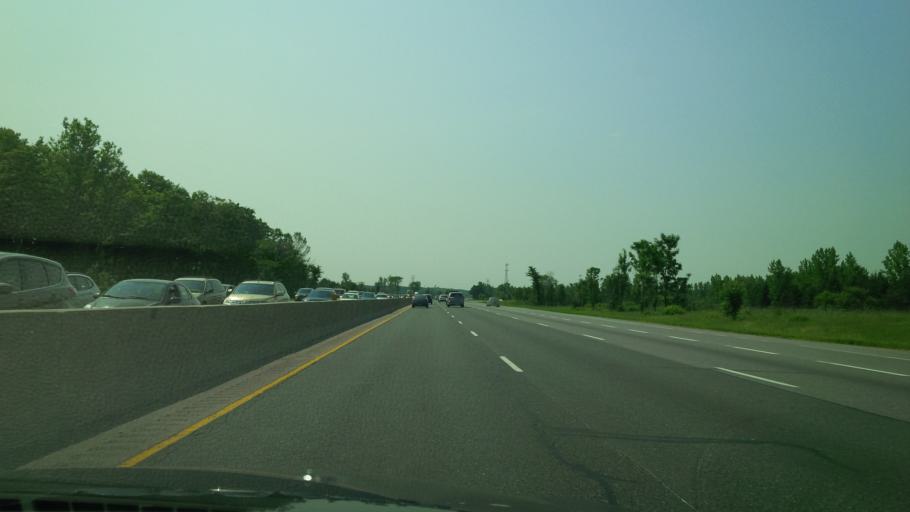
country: CA
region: Ontario
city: Bradford West Gwillimbury
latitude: 43.9995
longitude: -79.5854
